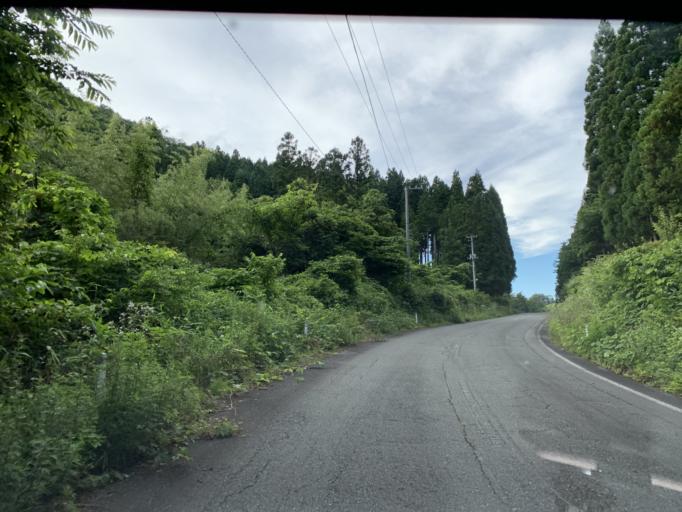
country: JP
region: Iwate
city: Ichinoseki
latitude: 38.8913
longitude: 140.9815
